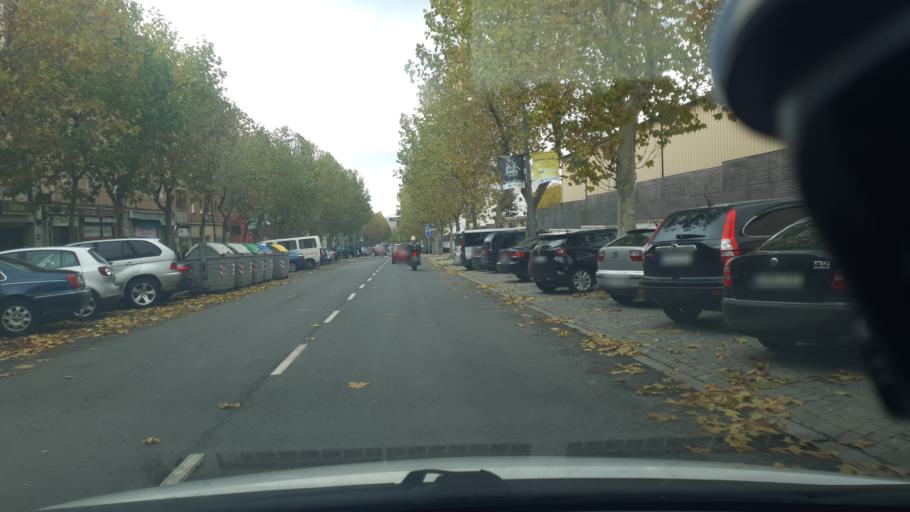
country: ES
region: Castille and Leon
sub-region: Provincia de Segovia
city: Segovia
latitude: 40.9387
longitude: -4.1120
